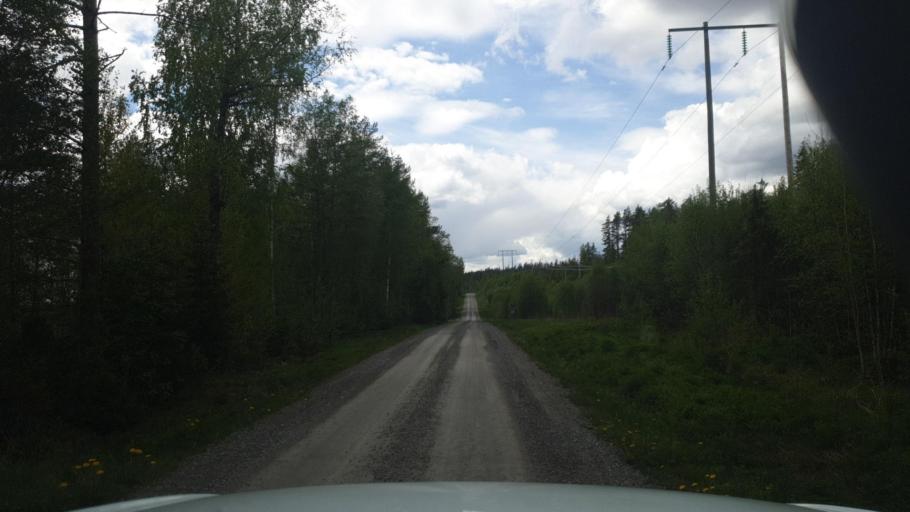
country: SE
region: Vaermland
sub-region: Arvika Kommun
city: Arvika
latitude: 59.5375
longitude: 12.4092
